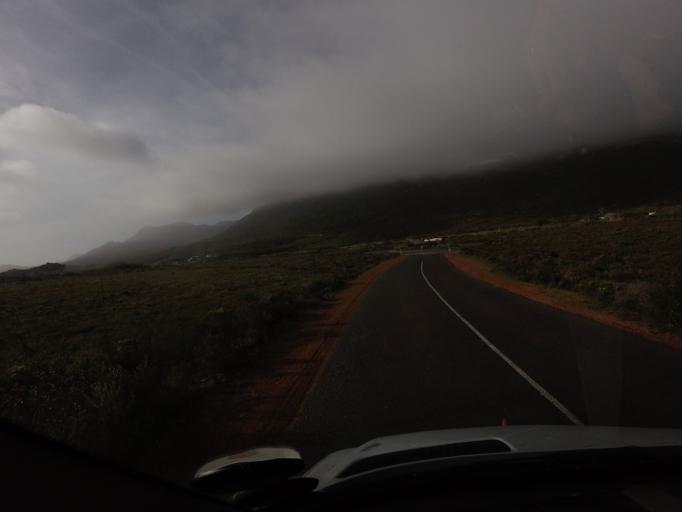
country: ZA
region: Western Cape
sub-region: City of Cape Town
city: Retreat
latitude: -34.2591
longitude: 18.4557
